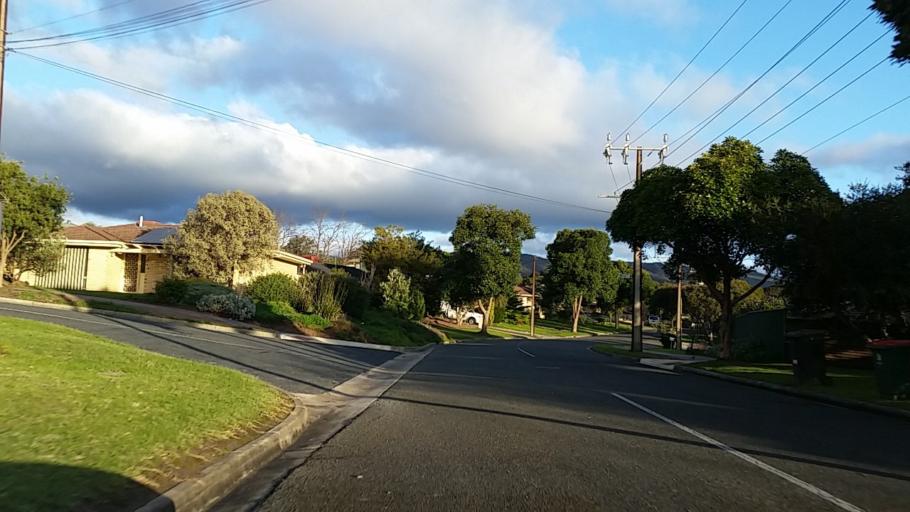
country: AU
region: South Australia
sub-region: Tea Tree Gully
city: Hope Valley
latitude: -34.8441
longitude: 138.7074
